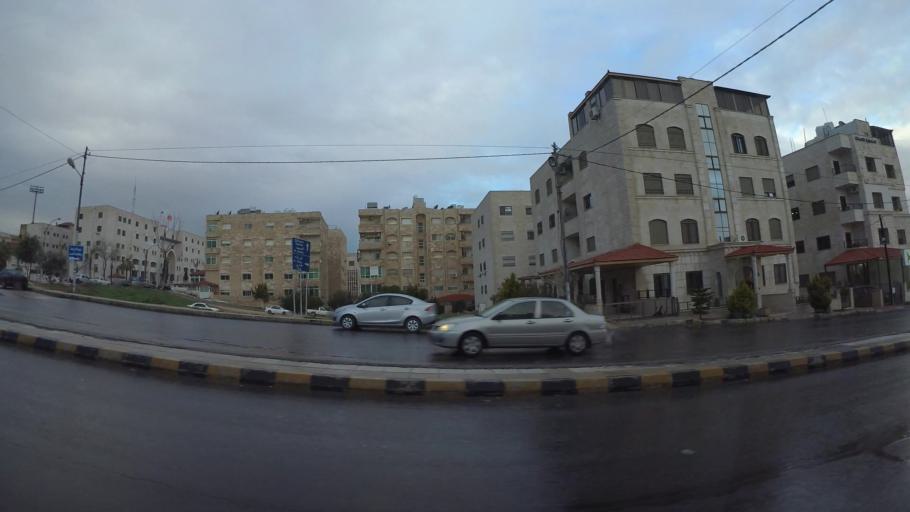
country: JO
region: Amman
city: Amman
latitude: 31.9788
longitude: 35.9115
